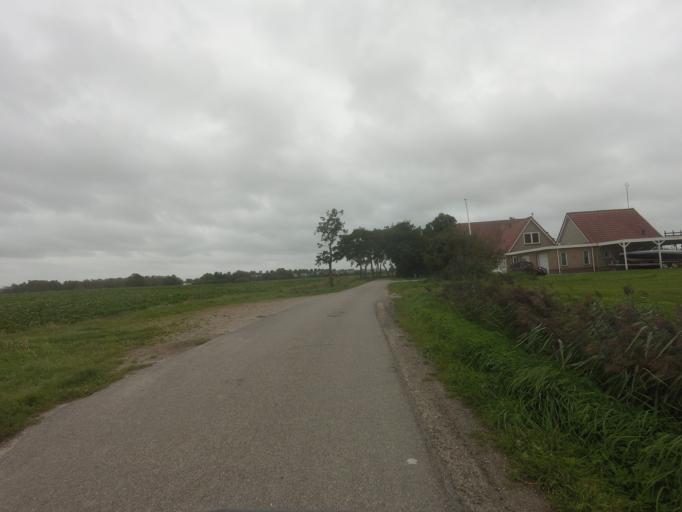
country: NL
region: Friesland
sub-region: Gemeente Leeuwarderadeel
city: Stiens
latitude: 53.2715
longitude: 5.7521
